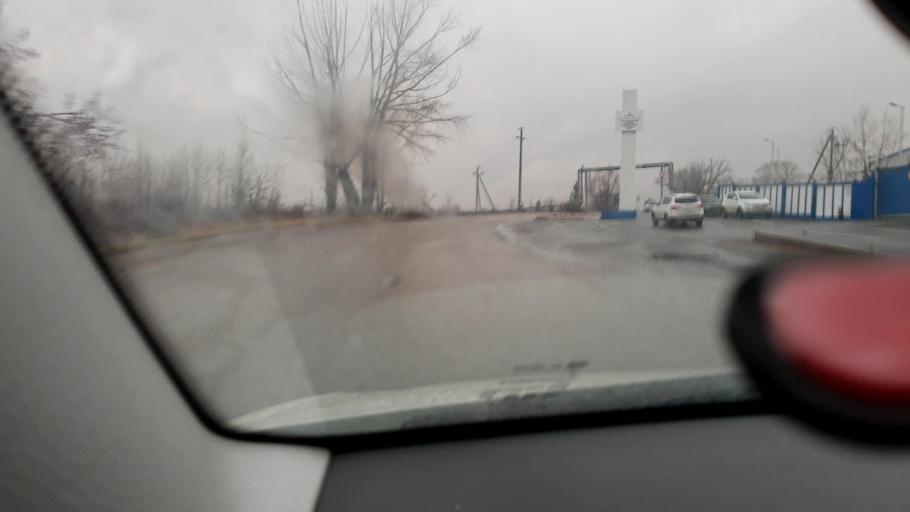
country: RU
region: Bashkortostan
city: Ufa
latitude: 54.8765
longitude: 56.1291
